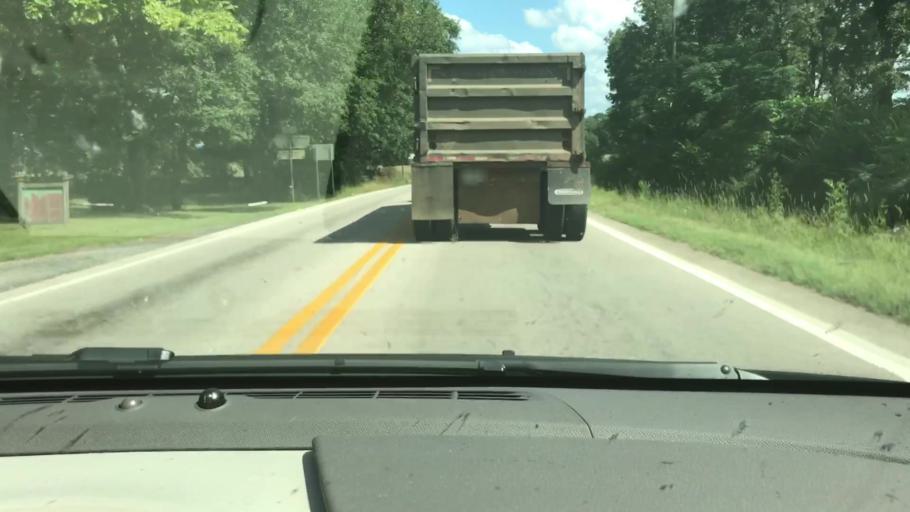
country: US
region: Georgia
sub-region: Troup County
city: West Point
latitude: 32.8701
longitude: -85.0351
